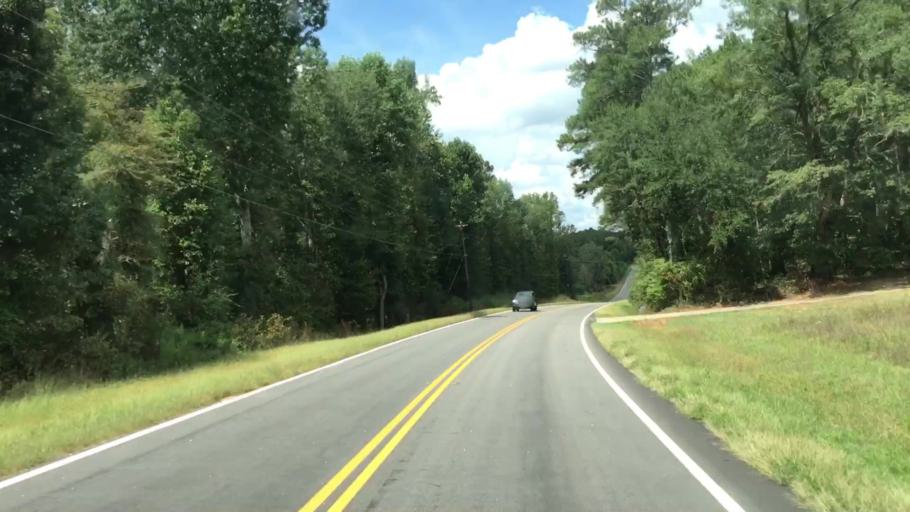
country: US
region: Georgia
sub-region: Greene County
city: Greensboro
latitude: 33.5599
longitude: -83.1371
